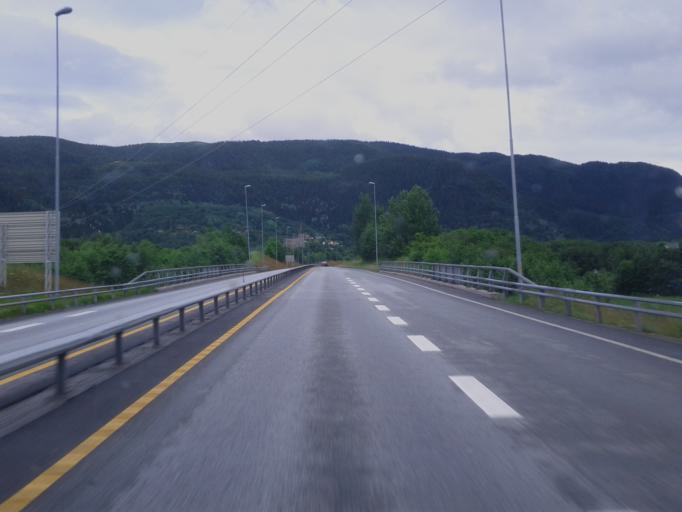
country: NO
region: Sor-Trondelag
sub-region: Melhus
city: Melhus
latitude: 63.2796
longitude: 10.2785
